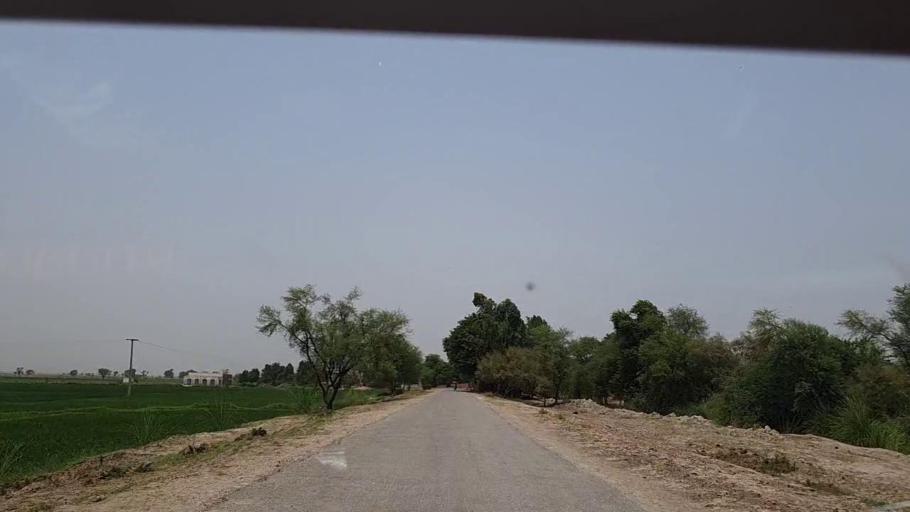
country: PK
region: Sindh
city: Khairpur Nathan Shah
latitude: 27.0157
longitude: 67.6702
